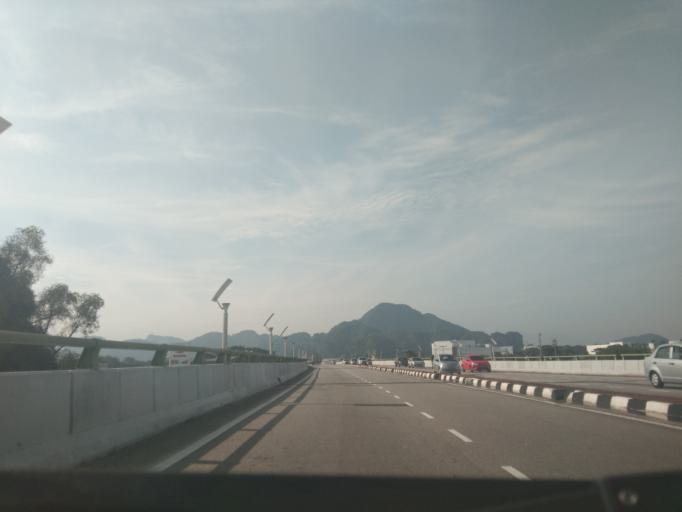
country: MY
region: Perak
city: Ipoh
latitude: 4.5800
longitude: 101.1043
